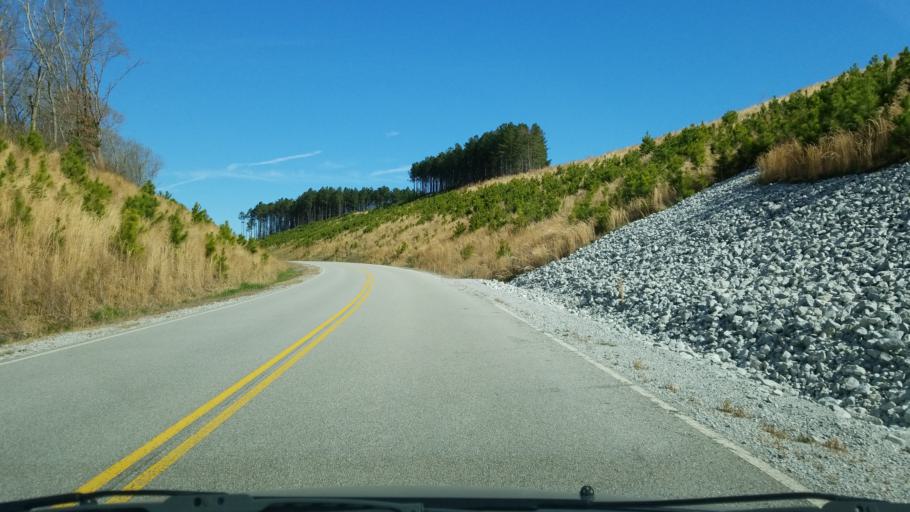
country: US
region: Tennessee
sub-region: Hamilton County
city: Harrison
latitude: 35.1001
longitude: -85.1366
